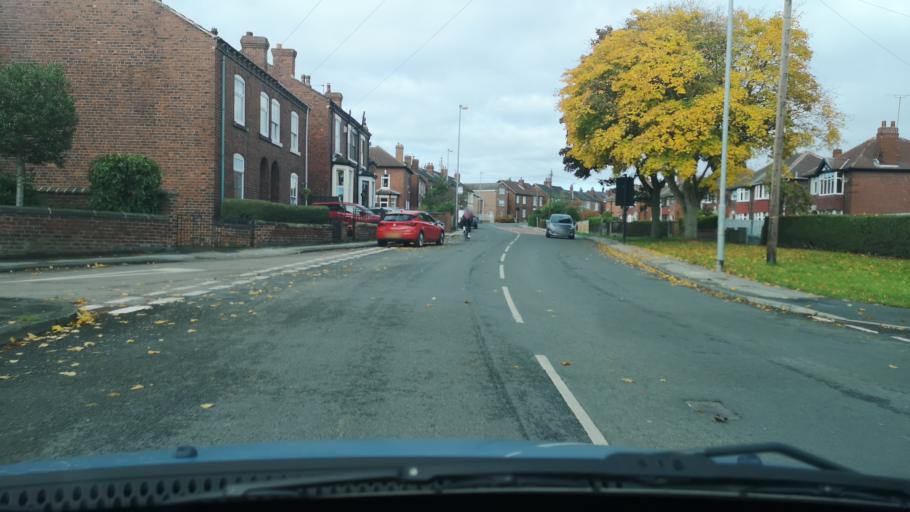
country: GB
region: England
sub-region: City and Borough of Wakefield
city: Normanton
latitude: 53.7050
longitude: -1.4342
